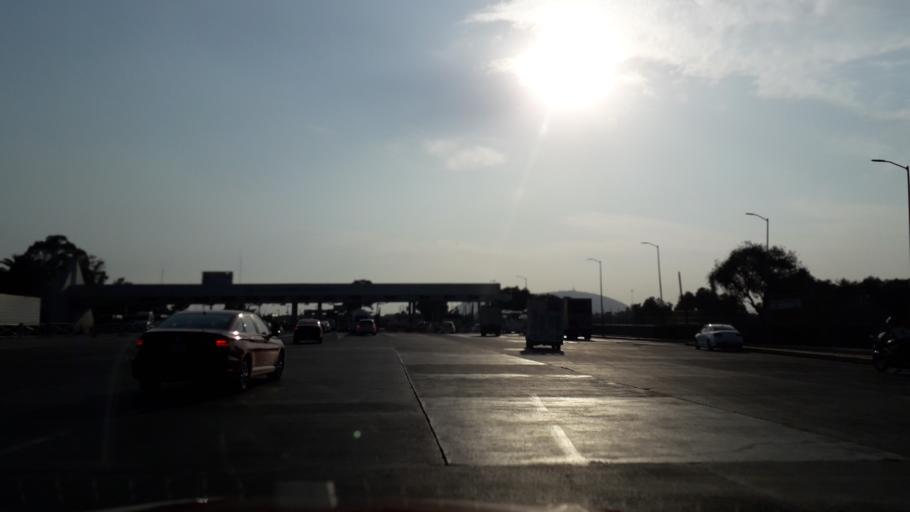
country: MX
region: Mexico
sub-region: Ixtapaluca
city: San Buenaventura
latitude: 19.2969
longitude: -98.8693
